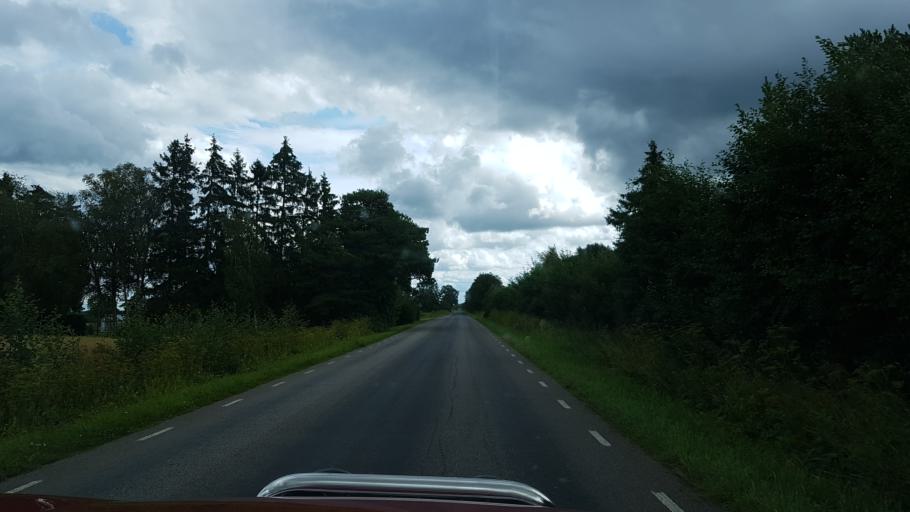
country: EE
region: Laeaene
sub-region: Lihula vald
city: Lihula
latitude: 58.7217
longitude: 23.9700
